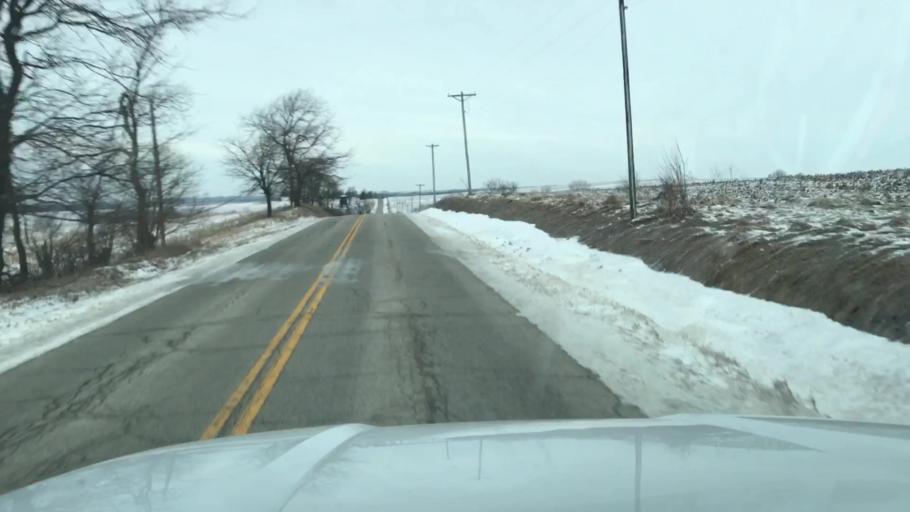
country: US
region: Missouri
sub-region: Andrew County
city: Savannah
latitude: 40.0249
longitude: -94.9436
